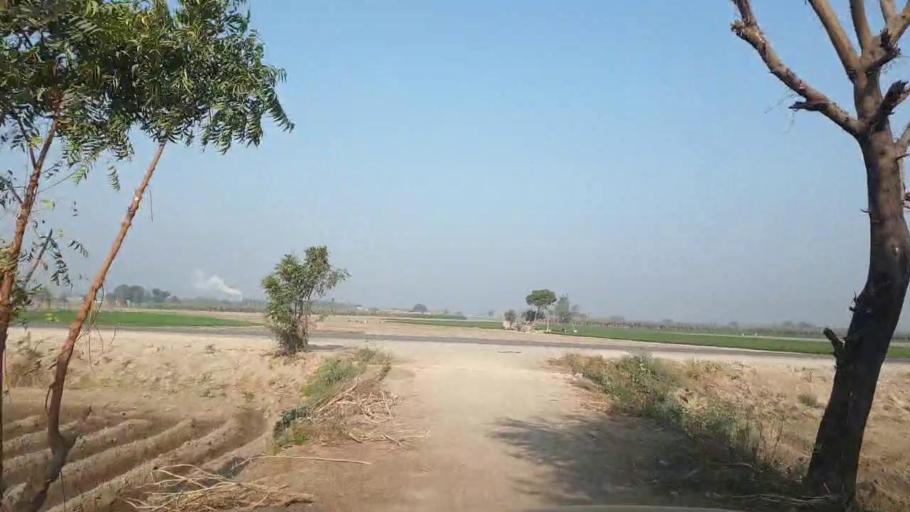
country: PK
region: Sindh
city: Tando Allahyar
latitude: 25.4776
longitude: 68.7366
